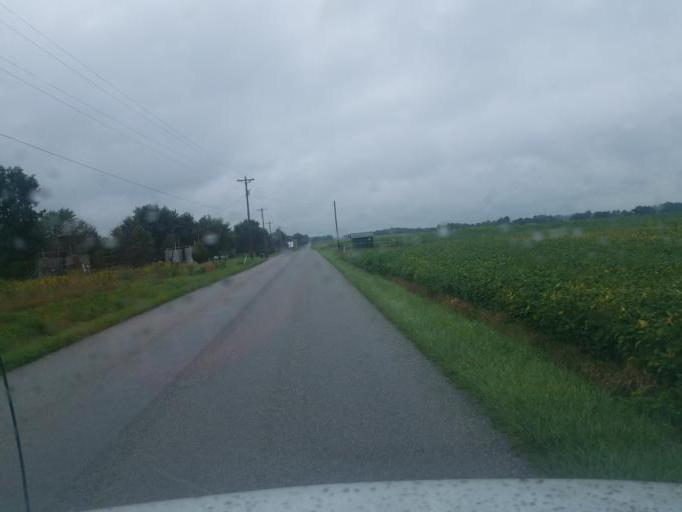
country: US
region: Ohio
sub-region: Medina County
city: Westfield Center
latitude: 40.9740
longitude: -81.9467
